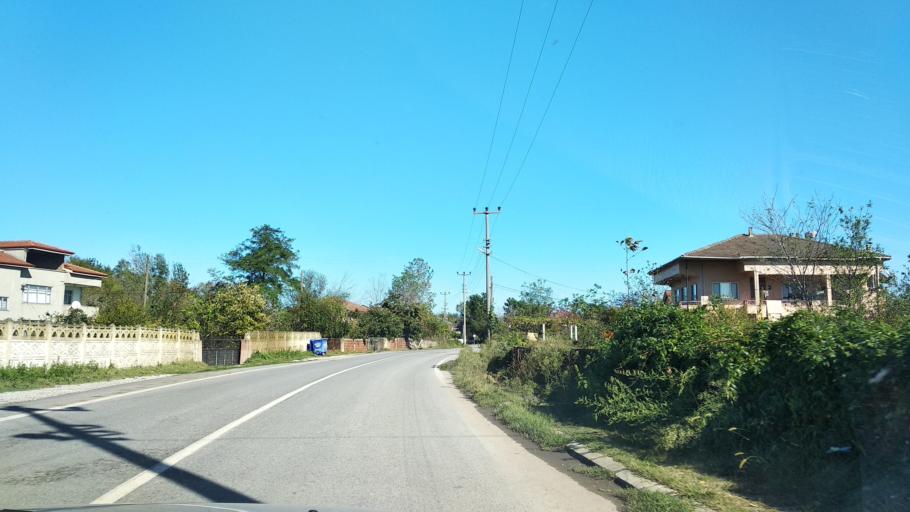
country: TR
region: Sakarya
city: Karasu
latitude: 41.1183
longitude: 30.6382
